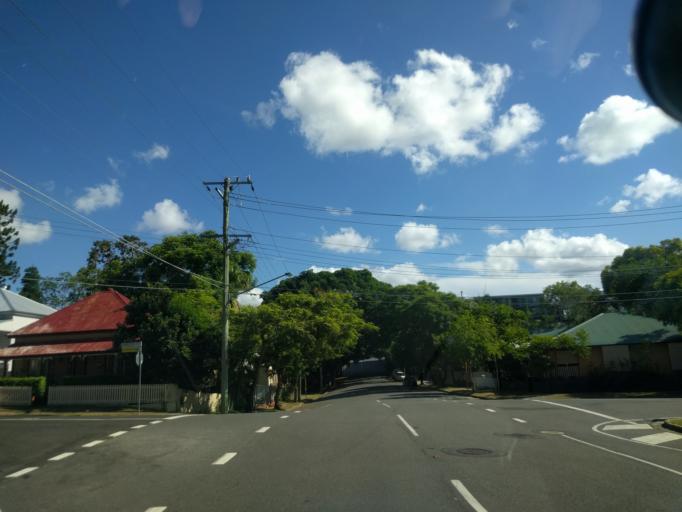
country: AU
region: Queensland
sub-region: Brisbane
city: Milton
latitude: -27.4607
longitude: 153.0093
